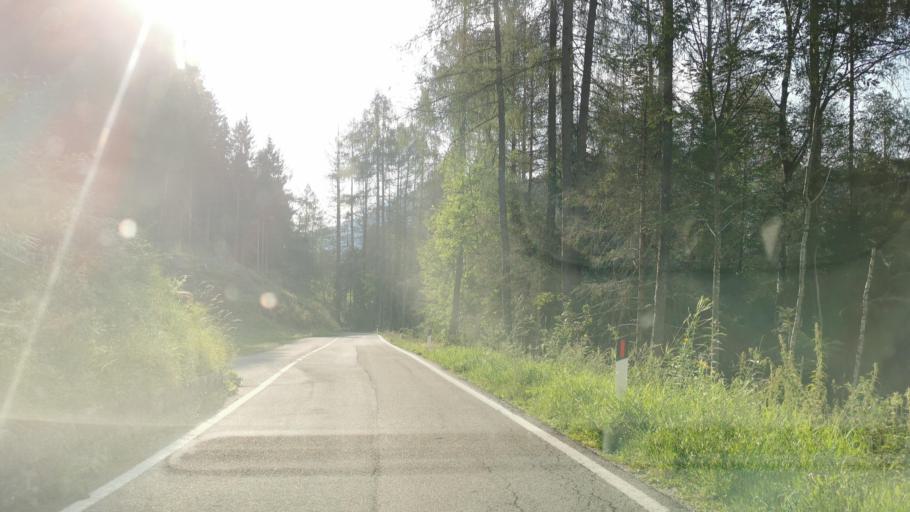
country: IT
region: Trentino-Alto Adige
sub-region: Provincia di Trento
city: Frassilongo
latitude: 46.0955
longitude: 11.3104
